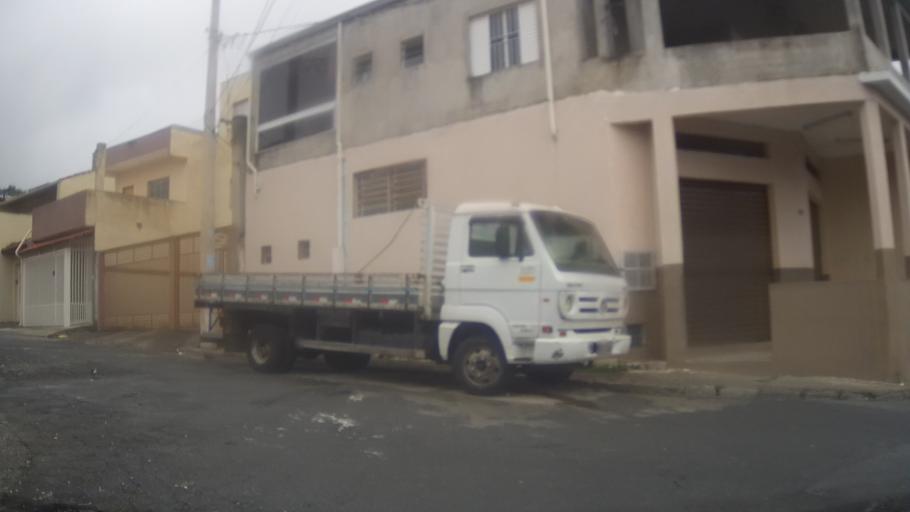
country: BR
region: Sao Paulo
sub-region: Guarulhos
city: Guarulhos
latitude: -23.4394
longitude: -46.5350
